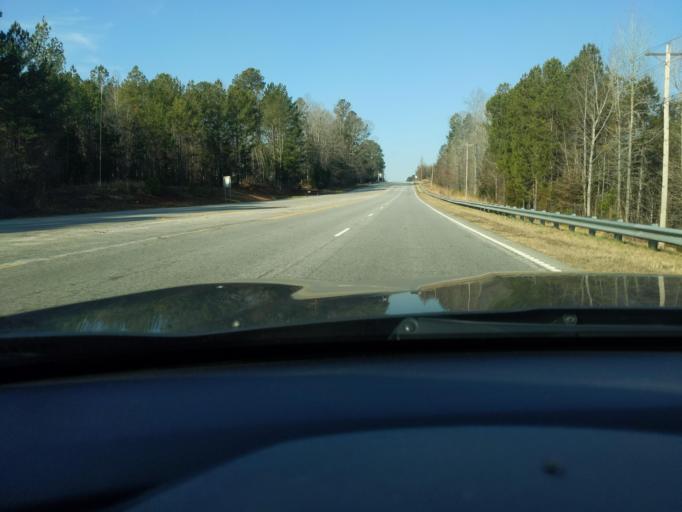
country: US
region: South Carolina
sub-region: Abbeville County
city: Abbeville
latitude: 34.1850
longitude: -82.3318
